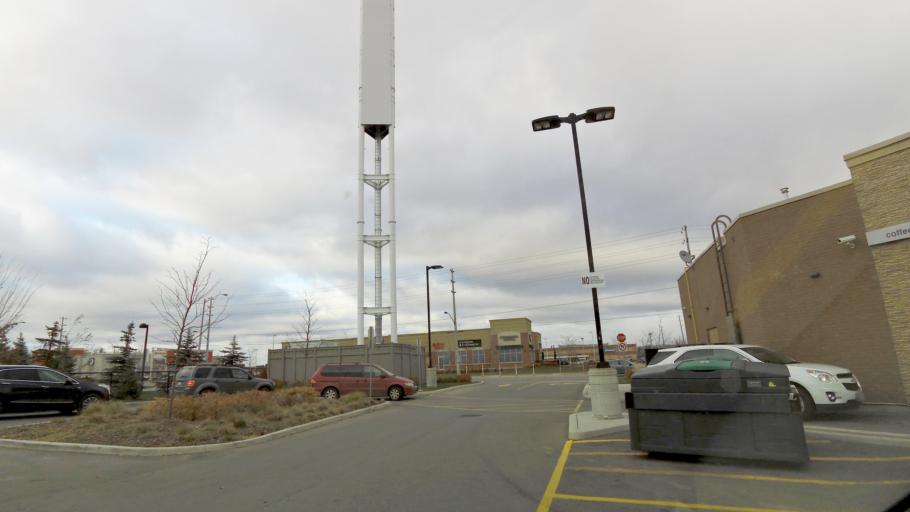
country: CA
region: Ontario
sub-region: Halton
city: Milton
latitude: 43.5064
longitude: -79.8384
